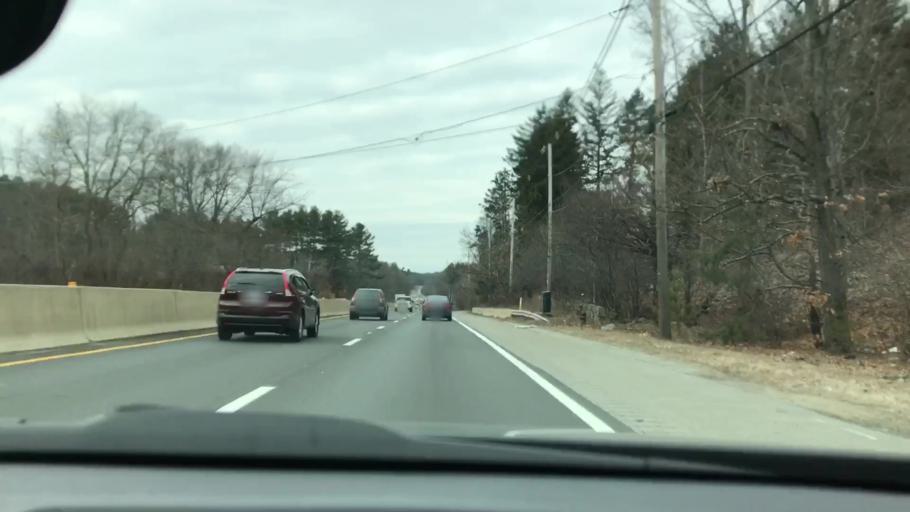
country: US
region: Massachusetts
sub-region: Middlesex County
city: Lincoln
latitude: 42.4350
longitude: -71.2748
